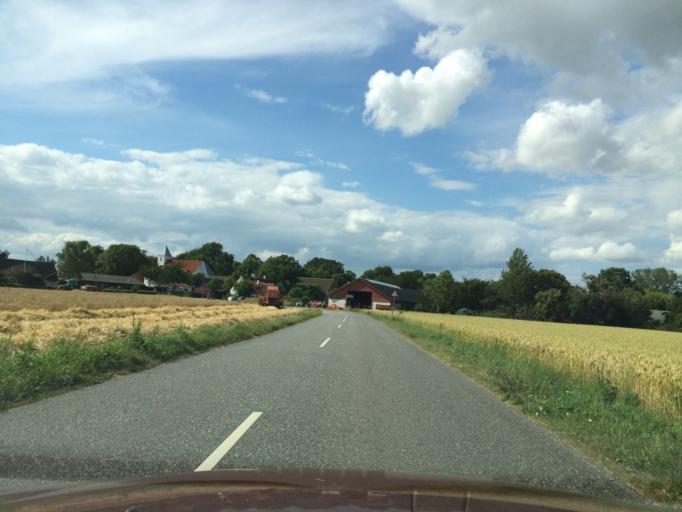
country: DK
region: Central Jutland
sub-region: Syddjurs Kommune
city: Ebeltoft
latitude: 56.3010
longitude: 10.6958
